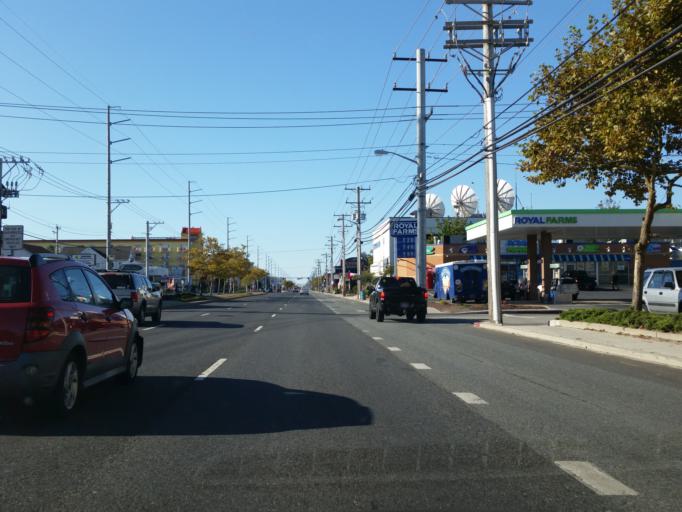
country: US
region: Maryland
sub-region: Worcester County
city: Ocean City
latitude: 38.4029
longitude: -75.0607
